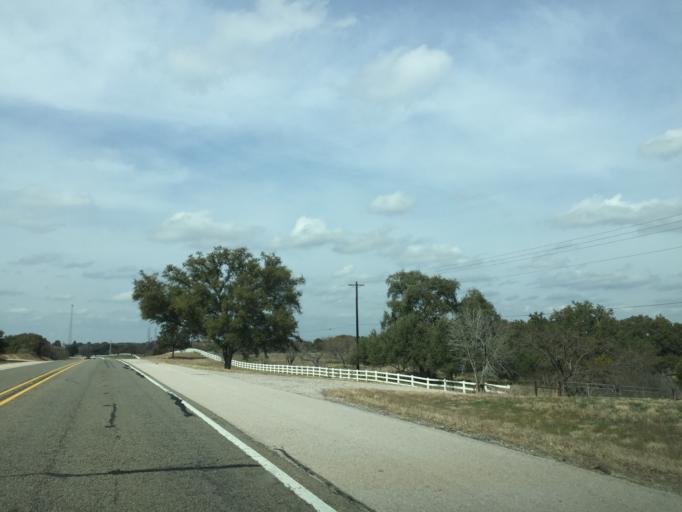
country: US
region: Texas
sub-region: Burnet County
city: Granite Shoals
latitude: 30.5231
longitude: -98.4154
